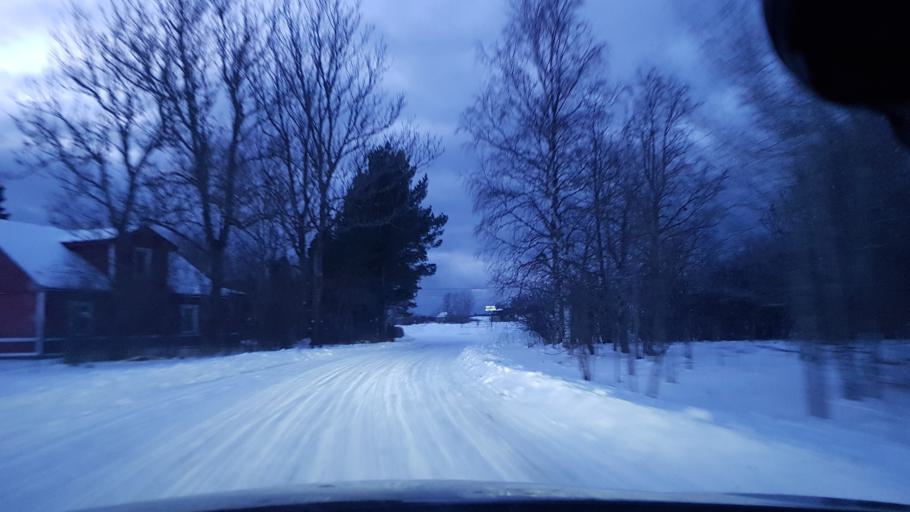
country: EE
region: Laeaene
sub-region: Haapsalu linn
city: Haapsalu
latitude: 59.2193
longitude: 23.5288
